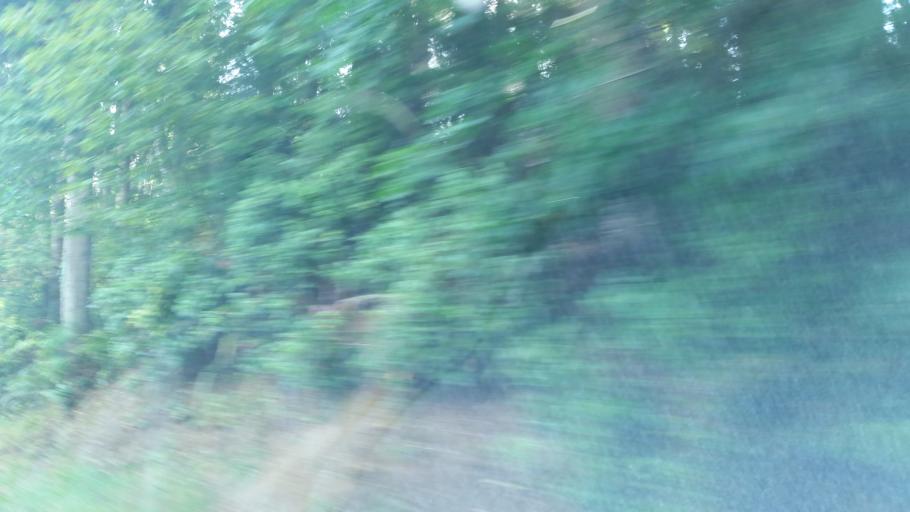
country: US
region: Oregon
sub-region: Clatsop County
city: Astoria
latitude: 46.1866
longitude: -123.8113
